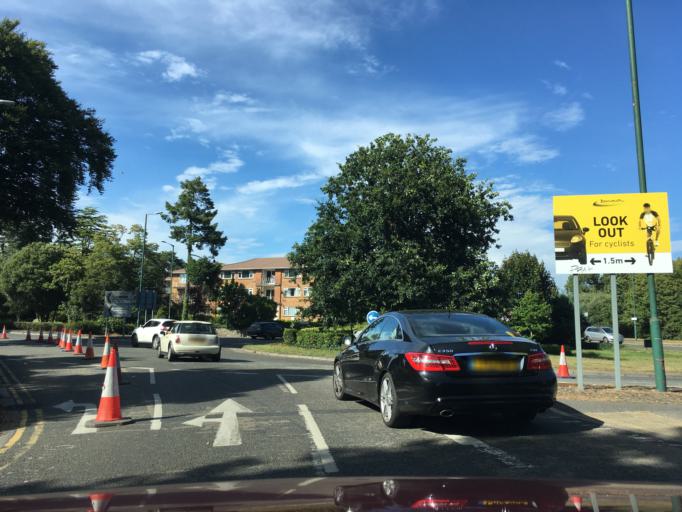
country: GB
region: England
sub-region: Bournemouth
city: Bournemouth
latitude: 50.7401
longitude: -1.8888
